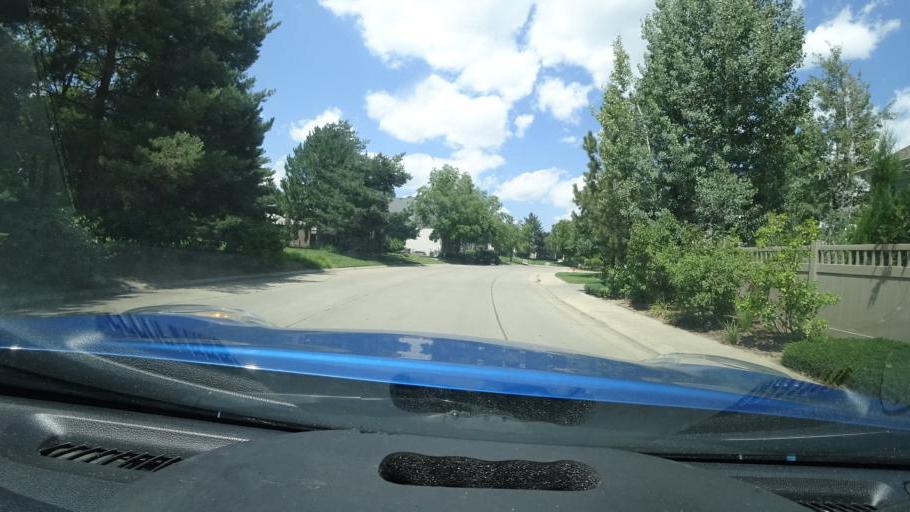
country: US
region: Colorado
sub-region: Arapahoe County
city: Glendale
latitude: 39.6985
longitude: -104.8935
